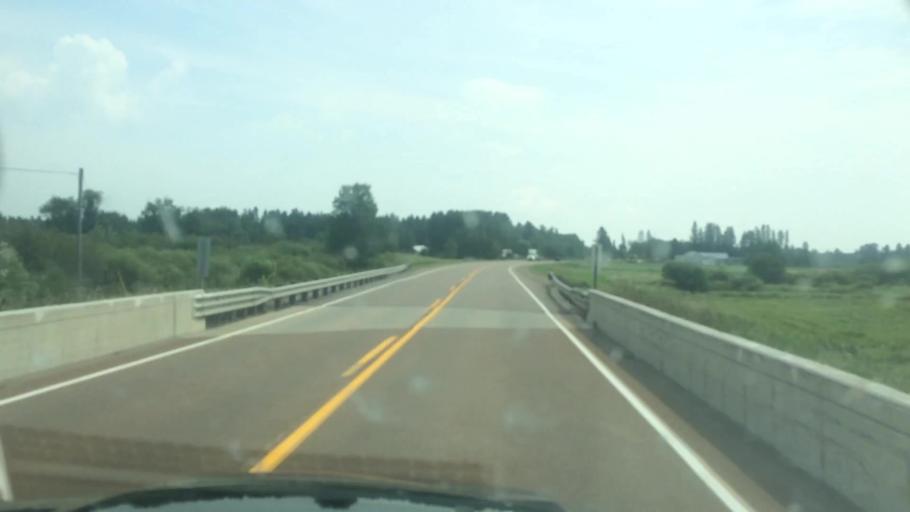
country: US
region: Wisconsin
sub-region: Langlade County
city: Antigo
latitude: 45.1465
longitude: -89.2812
